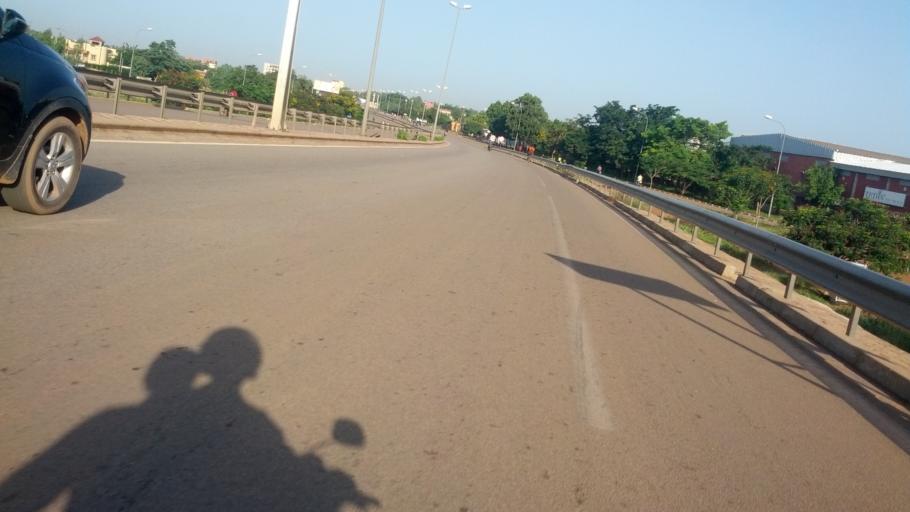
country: BF
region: Centre
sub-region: Kadiogo Province
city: Ouagadougou
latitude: 12.3327
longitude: -1.5040
